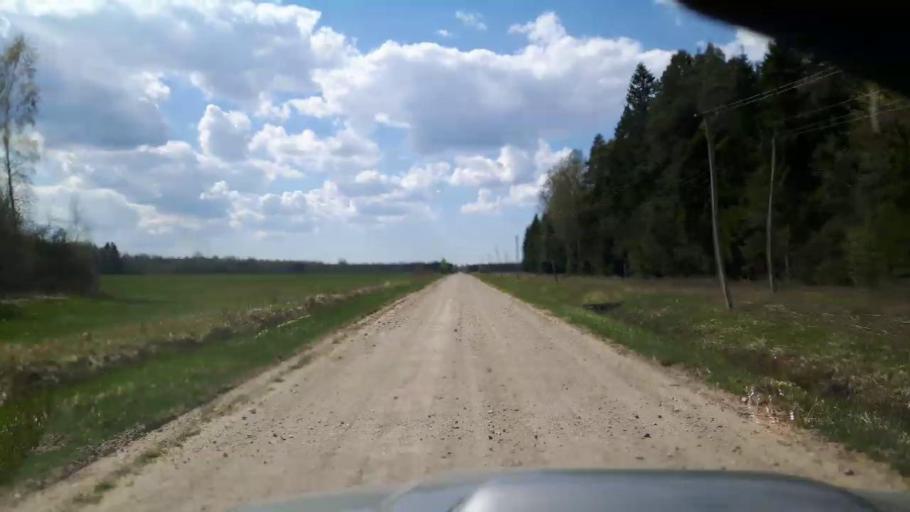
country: EE
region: Paernumaa
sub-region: Tootsi vald
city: Tootsi
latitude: 58.4658
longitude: 24.8916
